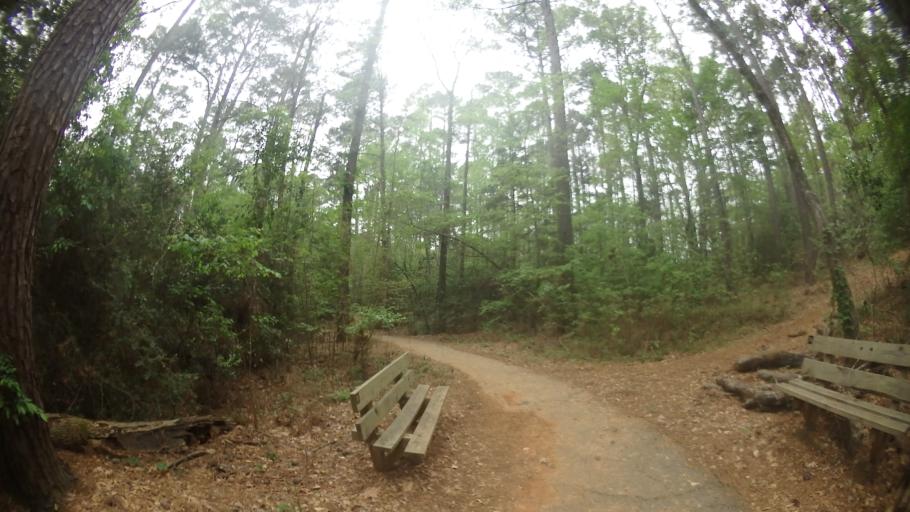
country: US
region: Texas
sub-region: Nacogdoches County
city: Nacogdoches
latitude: 31.6208
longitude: -94.6373
